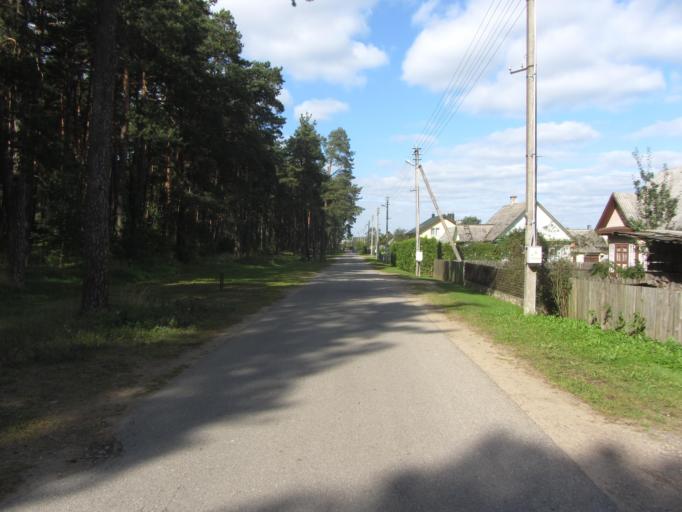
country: LT
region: Vilnius County
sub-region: Trakai
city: Rudiskes
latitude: 54.5168
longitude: 24.8229
